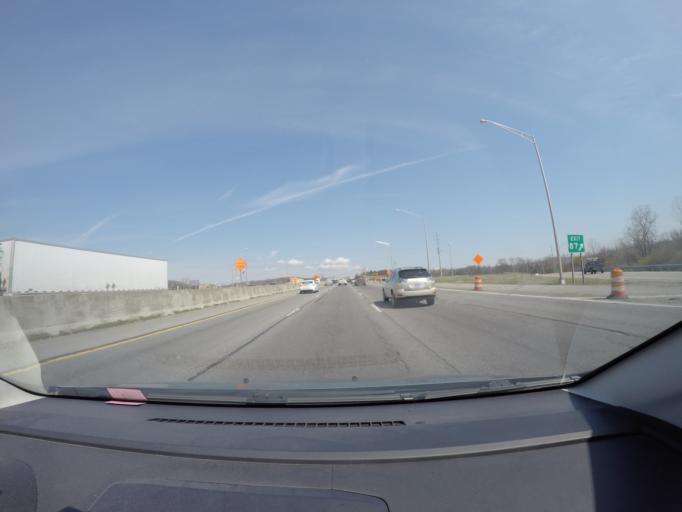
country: US
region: Tennessee
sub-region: Davidson County
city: Nashville
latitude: 36.2041
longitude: -86.7766
